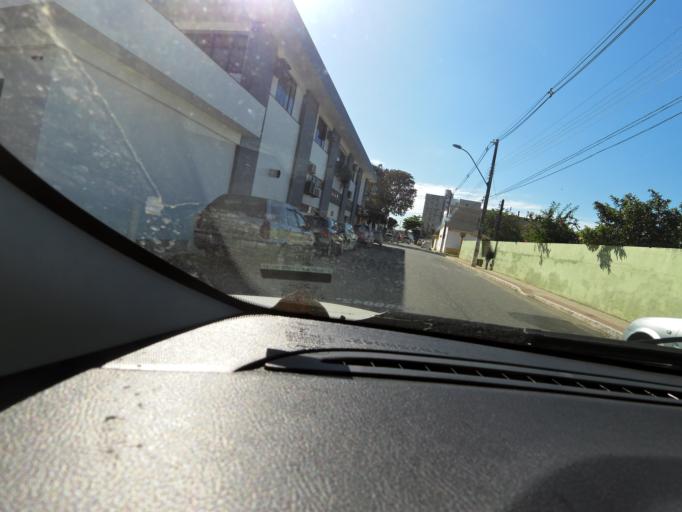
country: BR
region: Espirito Santo
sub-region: Guarapari
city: Guarapari
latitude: -20.6641
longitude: -40.5000
